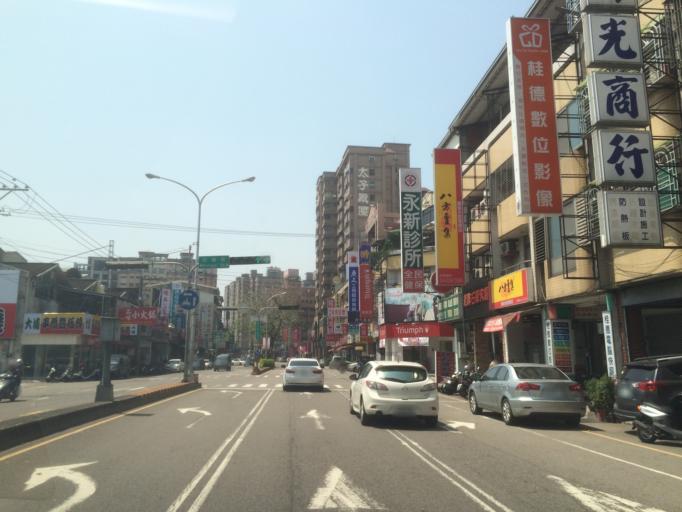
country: TW
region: Taiwan
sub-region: Taichung City
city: Taichung
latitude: 24.1829
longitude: 120.6987
